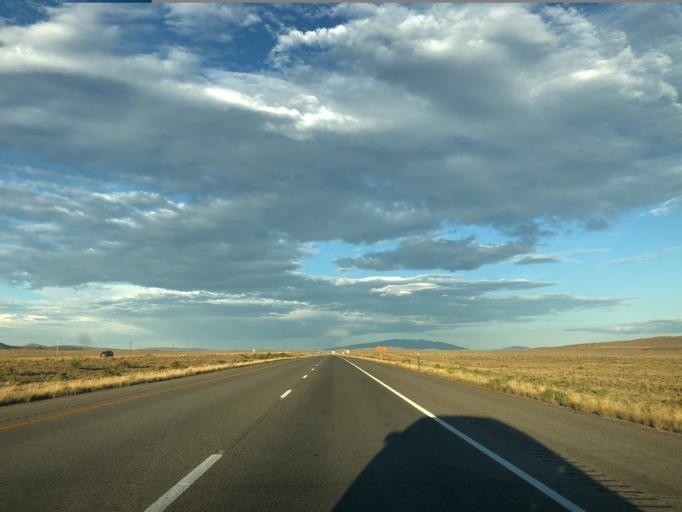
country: US
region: Wyoming
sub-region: Carbon County
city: Rawlins
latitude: 41.7627
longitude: -107.0105
